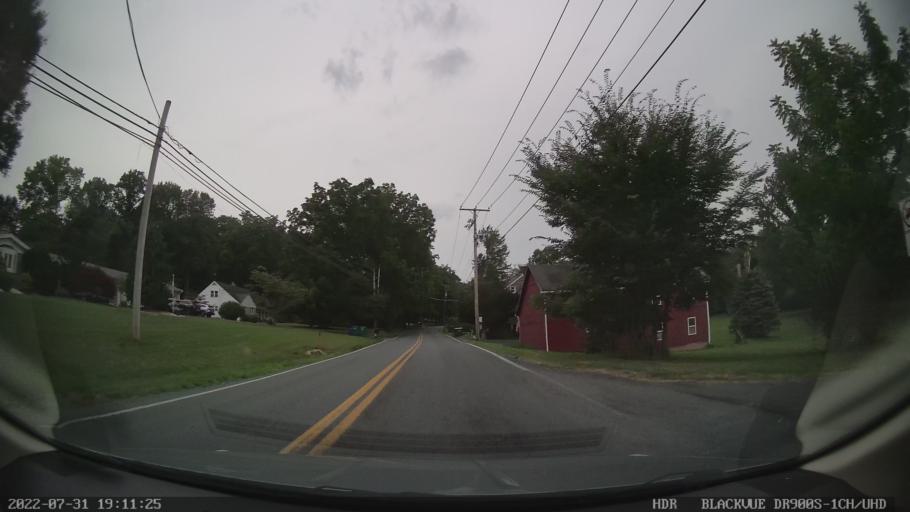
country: US
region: Pennsylvania
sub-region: Lehigh County
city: Fountain Hill
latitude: 40.5732
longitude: -75.3766
